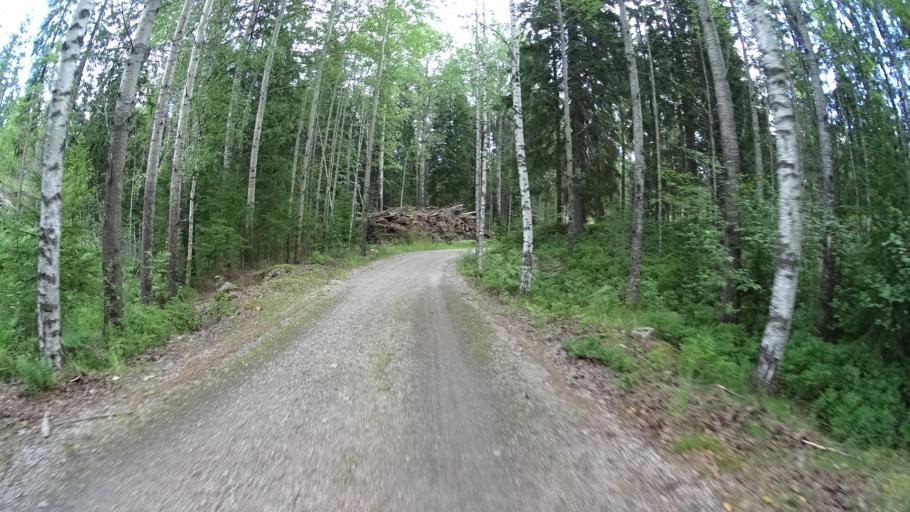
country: FI
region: Uusimaa
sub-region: Helsinki
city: Espoo
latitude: 60.2667
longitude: 24.6139
